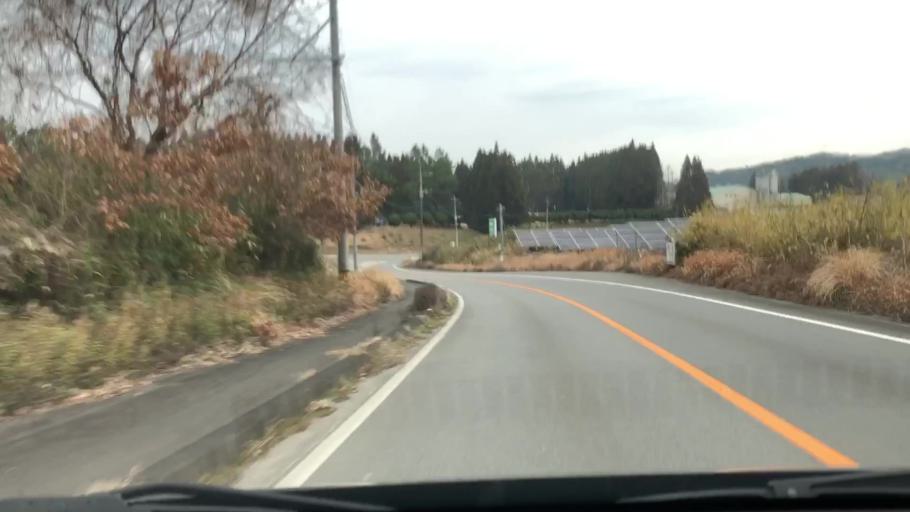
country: JP
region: Oita
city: Usuki
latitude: 33.0072
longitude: 131.6307
